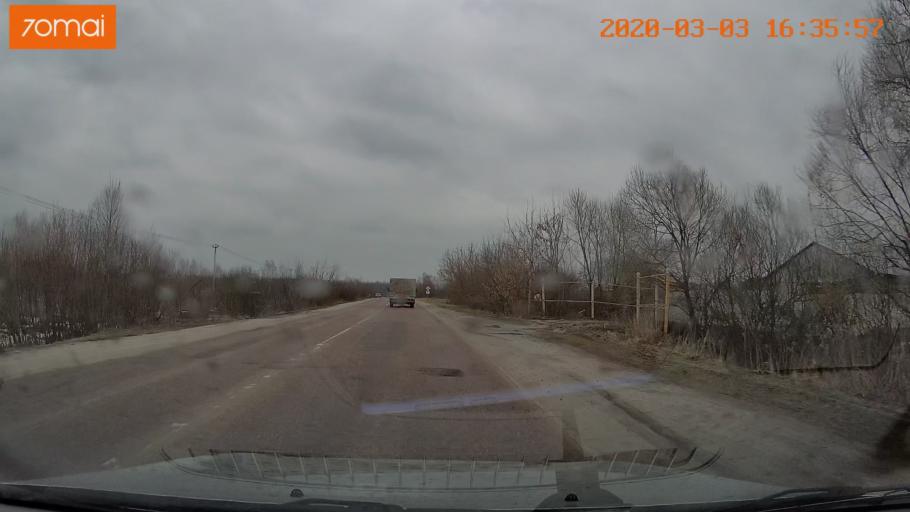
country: RU
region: Moskovskaya
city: Lopatinskiy
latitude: 55.4014
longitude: 38.7670
